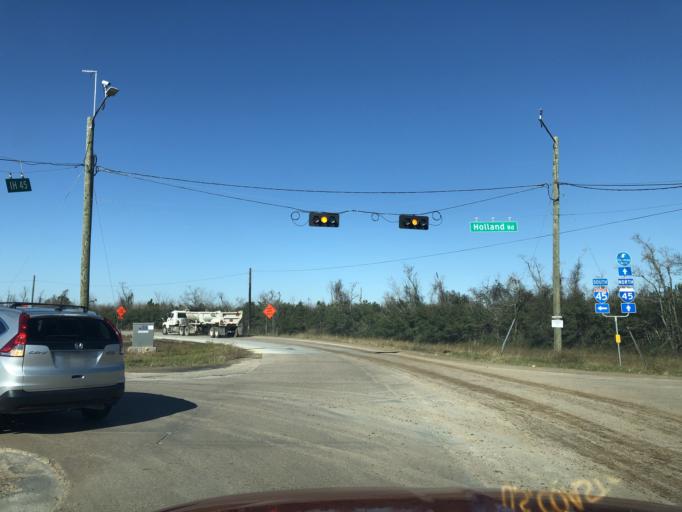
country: US
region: Texas
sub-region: Galveston County
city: Dickinson
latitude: 29.4303
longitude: -95.0574
